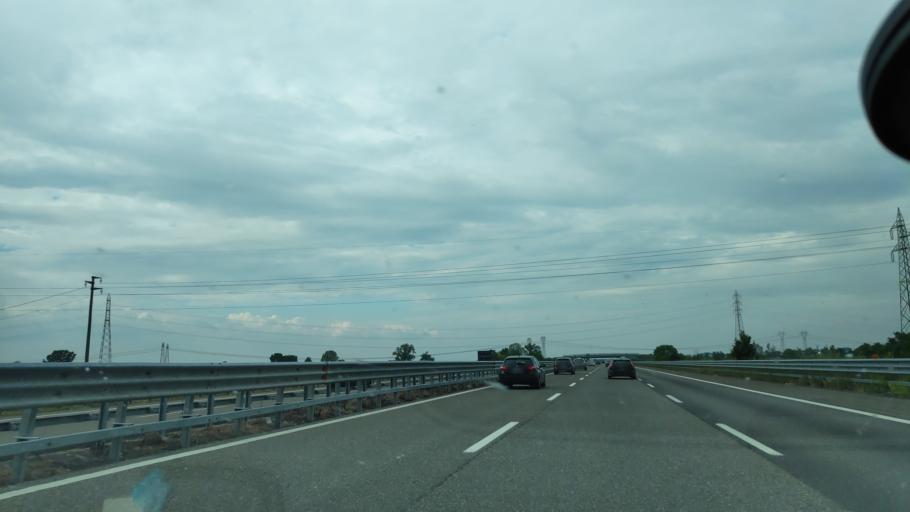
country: IT
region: Piedmont
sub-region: Provincia di Alessandria
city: Castelnuovo Scrivia
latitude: 44.9847
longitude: 8.9028
